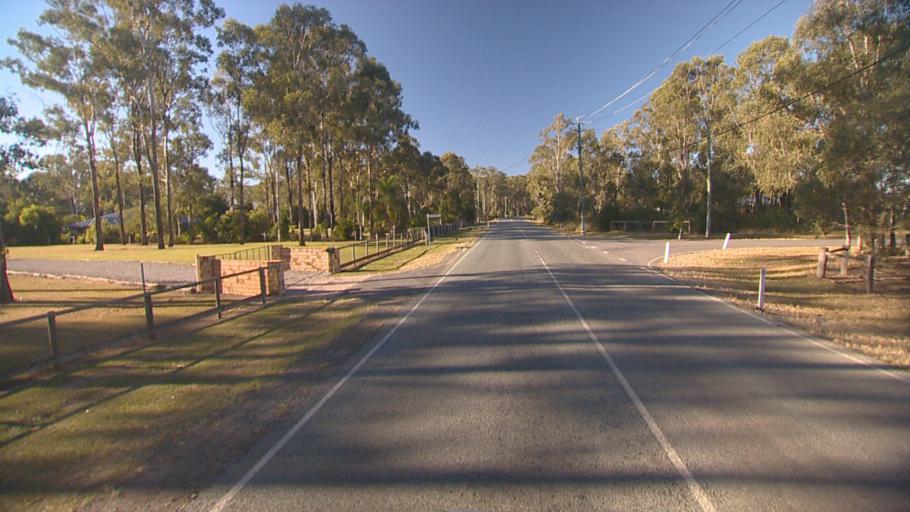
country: AU
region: Queensland
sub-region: Logan
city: Chambers Flat
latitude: -27.7483
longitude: 153.0586
